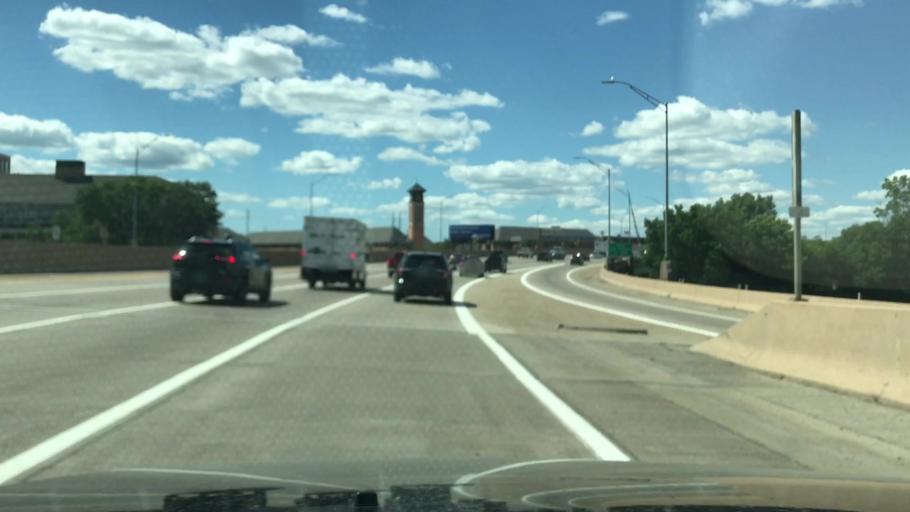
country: US
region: Michigan
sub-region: Kent County
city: Grand Rapids
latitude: 42.9613
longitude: -85.6766
